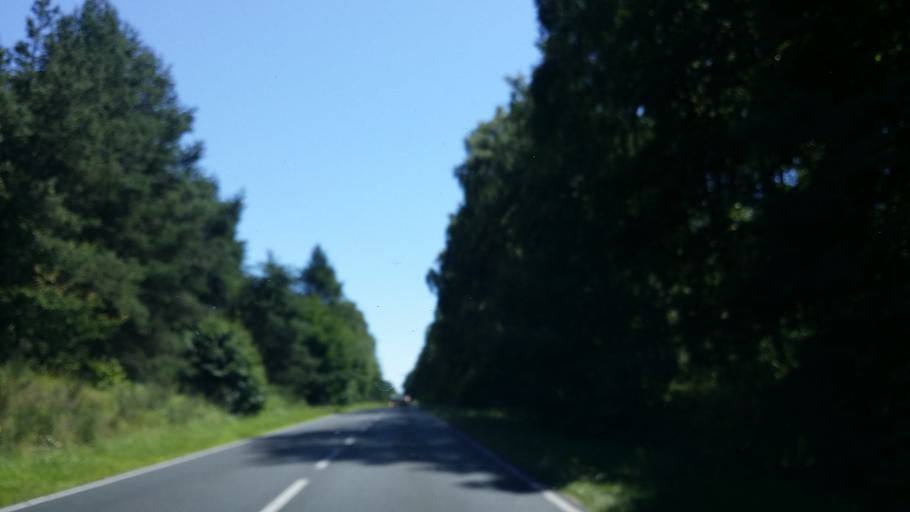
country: PL
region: West Pomeranian Voivodeship
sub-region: Powiat kolobrzeski
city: Kolobrzeg
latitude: 54.1208
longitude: 15.5835
